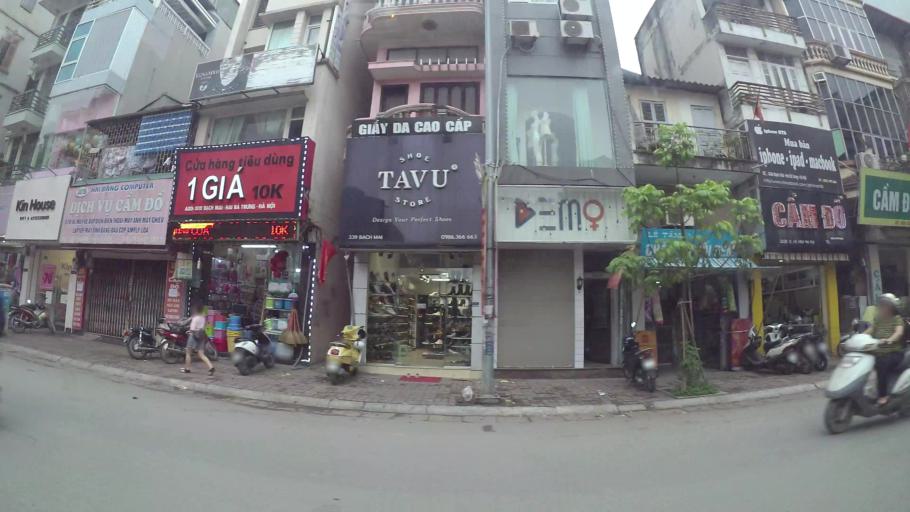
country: VN
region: Ha Noi
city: Hai BaTrung
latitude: 21.0006
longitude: 105.8506
